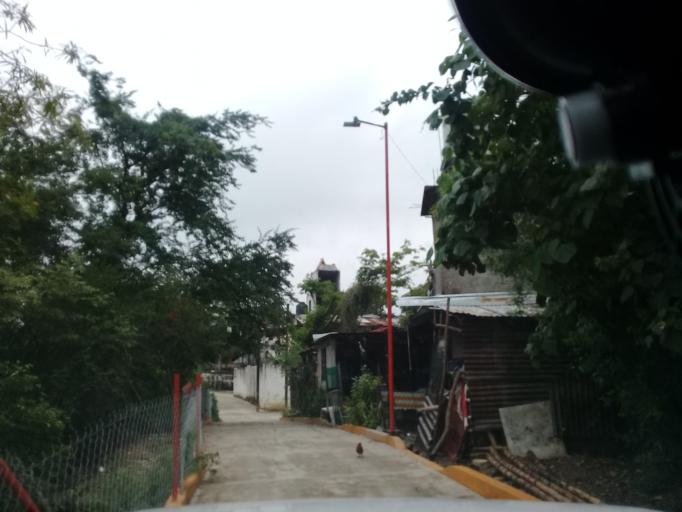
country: MX
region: Veracruz
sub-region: Chalma
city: San Pedro Coyutla
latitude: 21.2065
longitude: -98.3955
